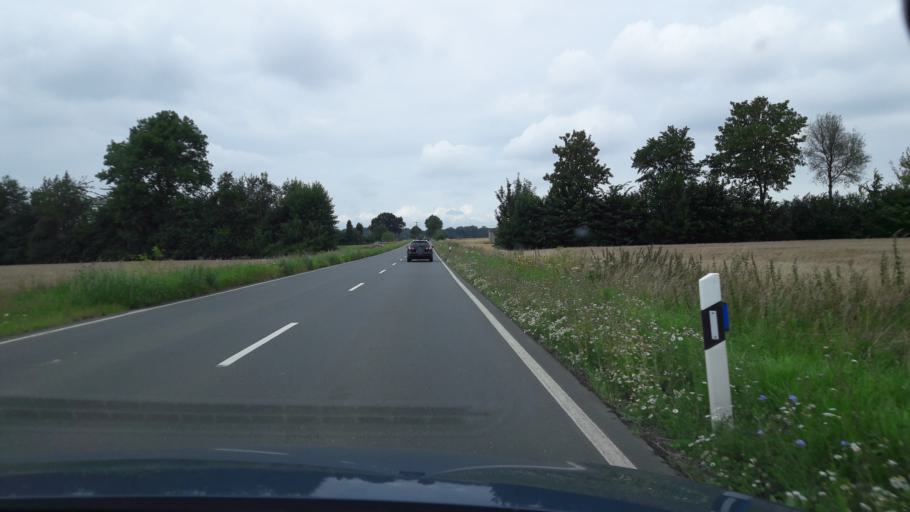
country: DE
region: North Rhine-Westphalia
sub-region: Regierungsbezirk Munster
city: Ennigerloh
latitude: 51.8442
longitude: 8.0029
